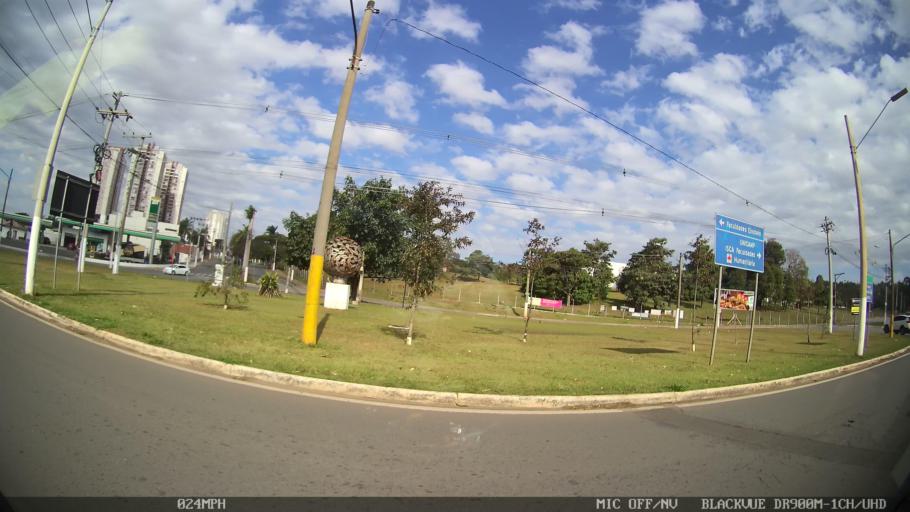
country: BR
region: Sao Paulo
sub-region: Limeira
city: Limeira
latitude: -22.5451
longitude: -47.4217
